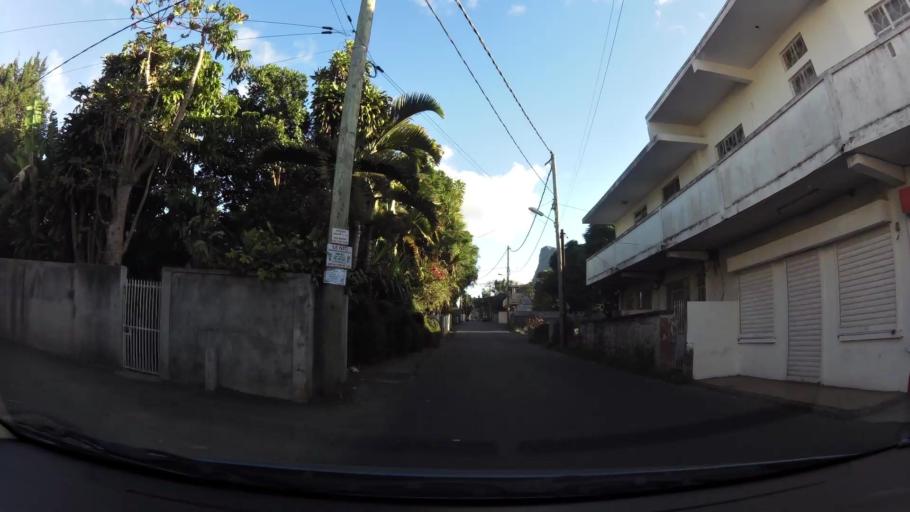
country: MU
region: Plaines Wilhems
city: Quatre Bornes
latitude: -20.2534
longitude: 57.4717
